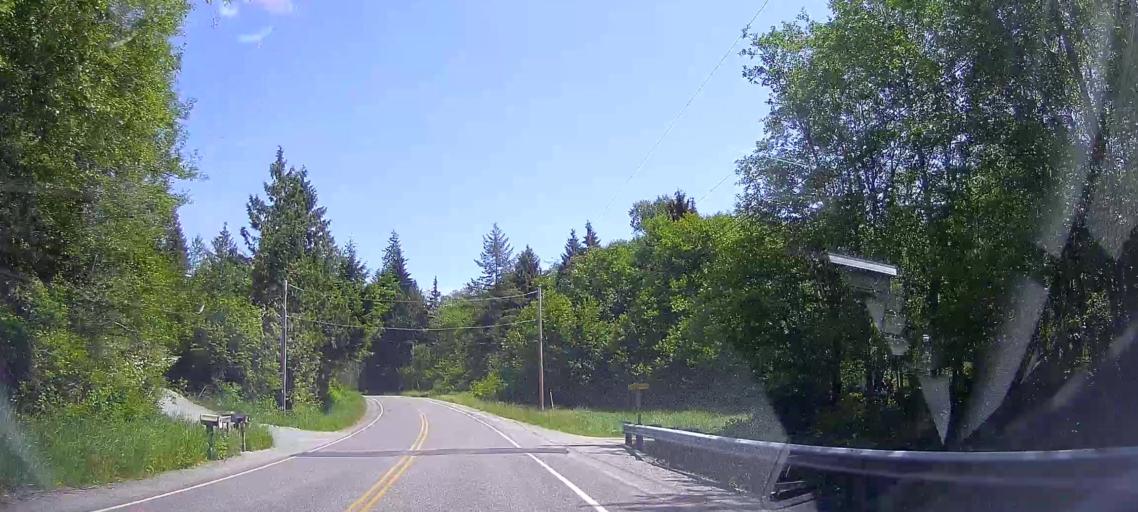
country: US
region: Washington
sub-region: Skagit County
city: Big Lake
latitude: 48.3923
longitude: -122.2643
